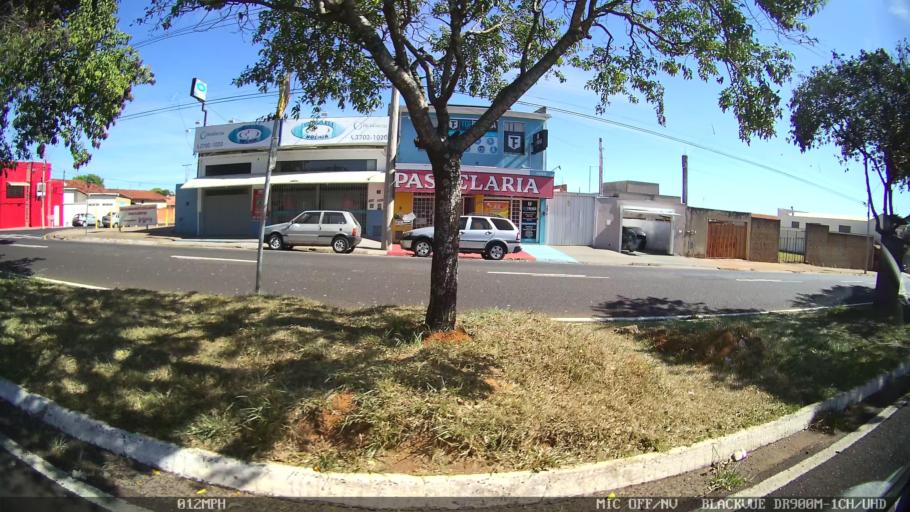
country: BR
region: Sao Paulo
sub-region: Franca
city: Franca
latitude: -20.5566
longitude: -47.3722
